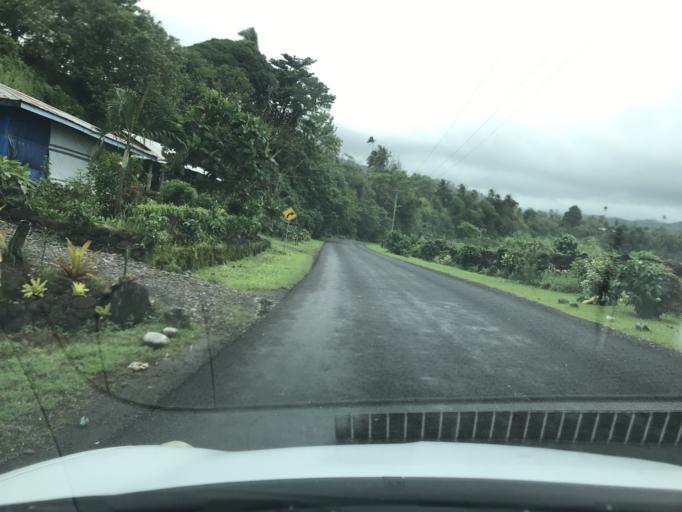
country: WS
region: Atua
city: Solosolo
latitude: -13.8743
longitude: -171.6427
